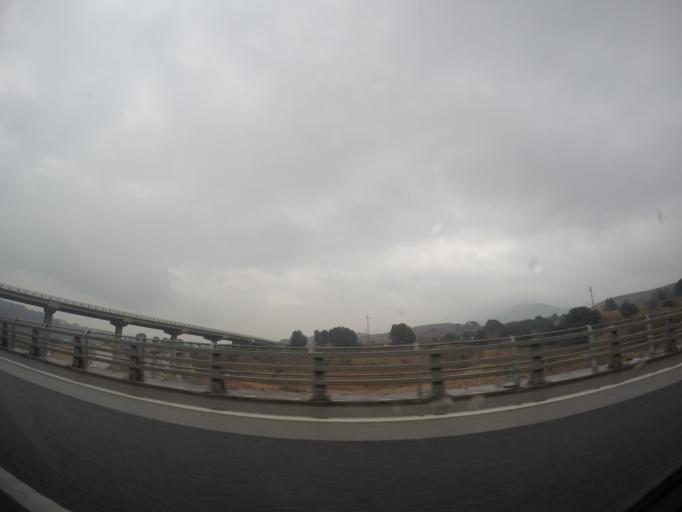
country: ES
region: Catalonia
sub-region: Provincia de Barcelona
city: Palleja
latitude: 41.4444
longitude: 1.9981
